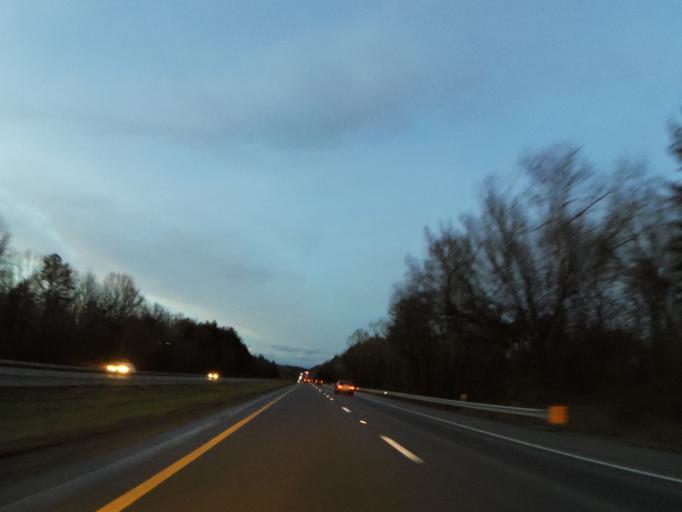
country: US
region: Kentucky
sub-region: Whitley County
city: Williamsburg
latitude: 36.7647
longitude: -84.1700
